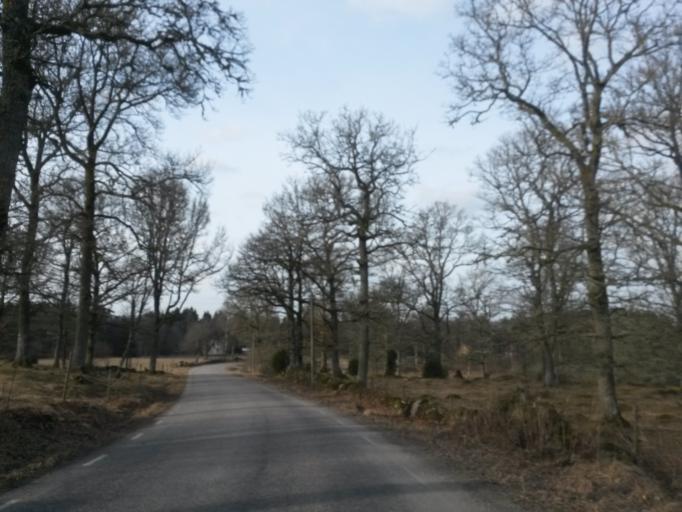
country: SE
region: Vaestra Goetaland
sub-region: Vargarda Kommun
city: Jonstorp
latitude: 57.9990
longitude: 12.7610
